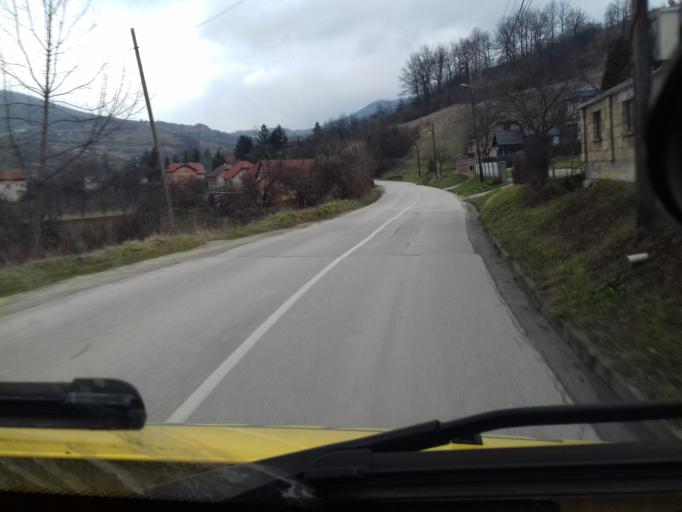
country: BA
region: Federation of Bosnia and Herzegovina
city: Zenica
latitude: 44.1793
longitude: 17.9662
